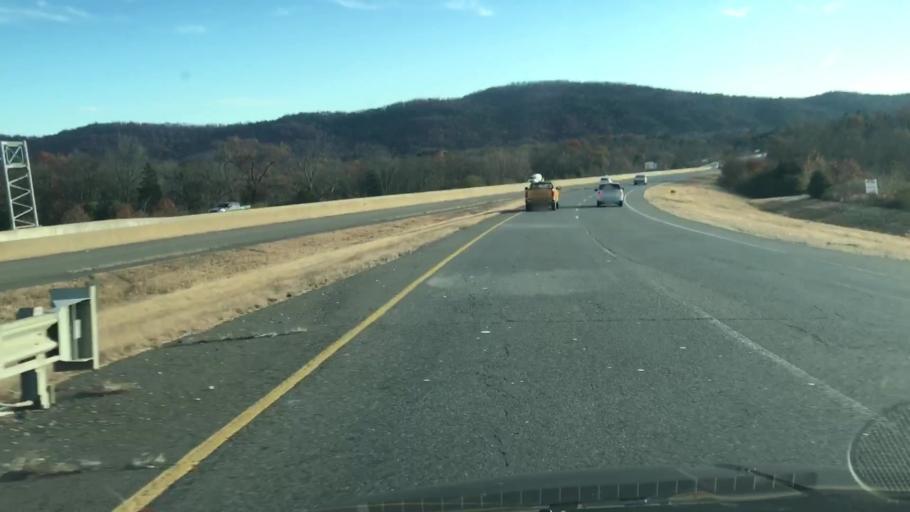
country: US
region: Arkansas
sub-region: Garland County
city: Hot Springs National Park
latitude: 34.5023
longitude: -92.9757
